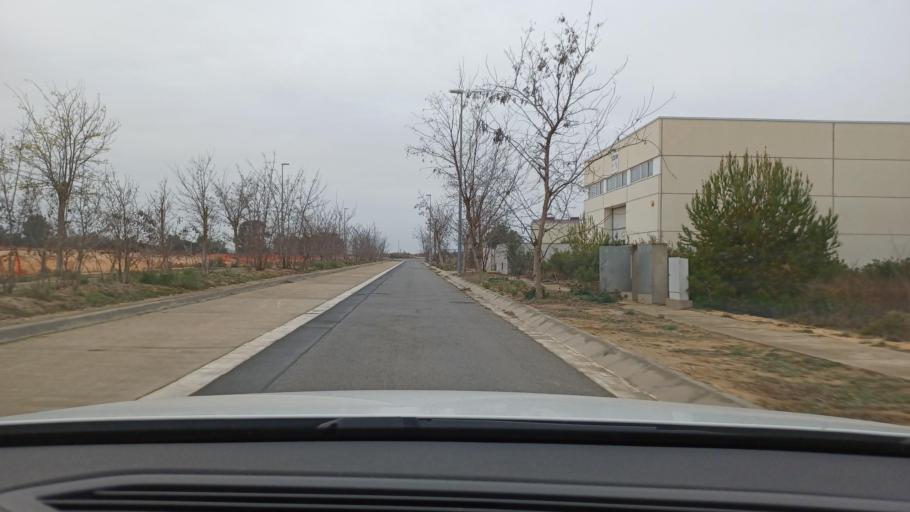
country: ES
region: Catalonia
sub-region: Provincia de Tarragona
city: Amposta
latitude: 40.7645
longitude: 0.5914
